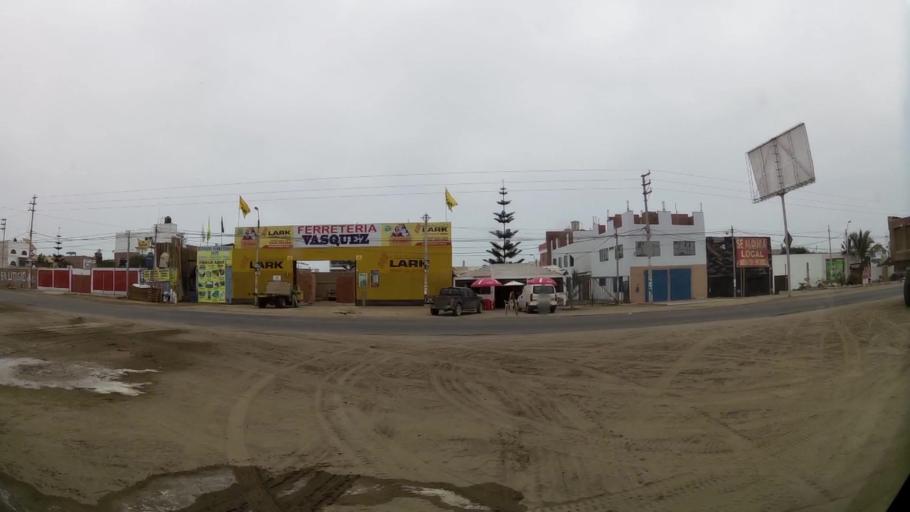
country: PE
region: Lima
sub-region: Lima
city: Punta Hermosa
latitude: -12.3081
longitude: -76.8383
